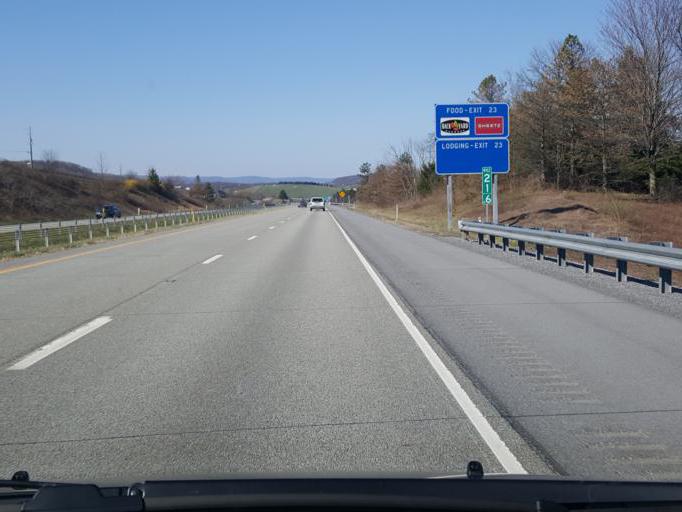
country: US
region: Pennsylvania
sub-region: Blair County
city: Roaring Spring
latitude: 40.3523
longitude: -78.4338
